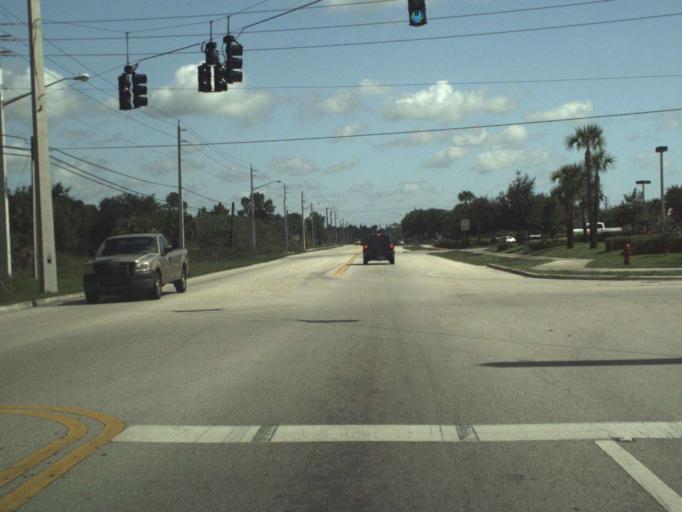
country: US
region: Florida
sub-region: Saint Lucie County
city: Port Saint Lucie
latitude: 27.2468
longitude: -80.3768
